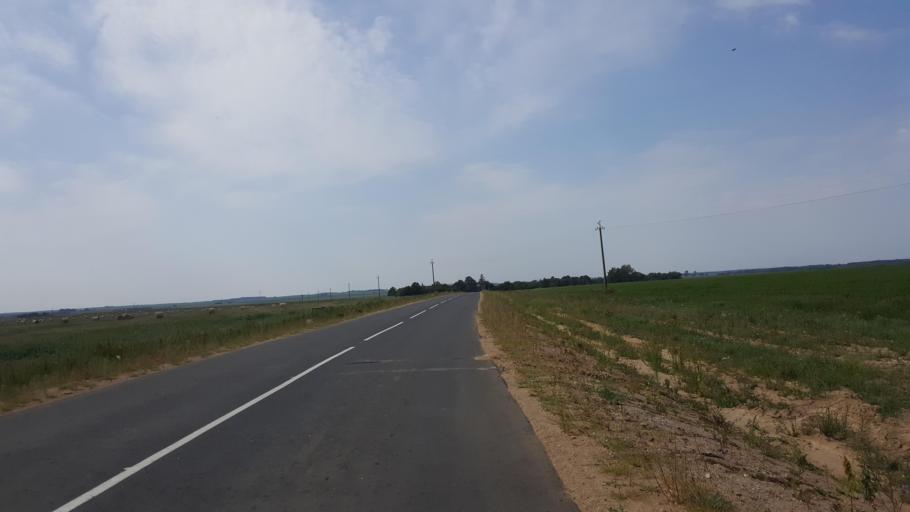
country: BY
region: Brest
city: Kamyanyets
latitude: 52.4545
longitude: 23.6639
